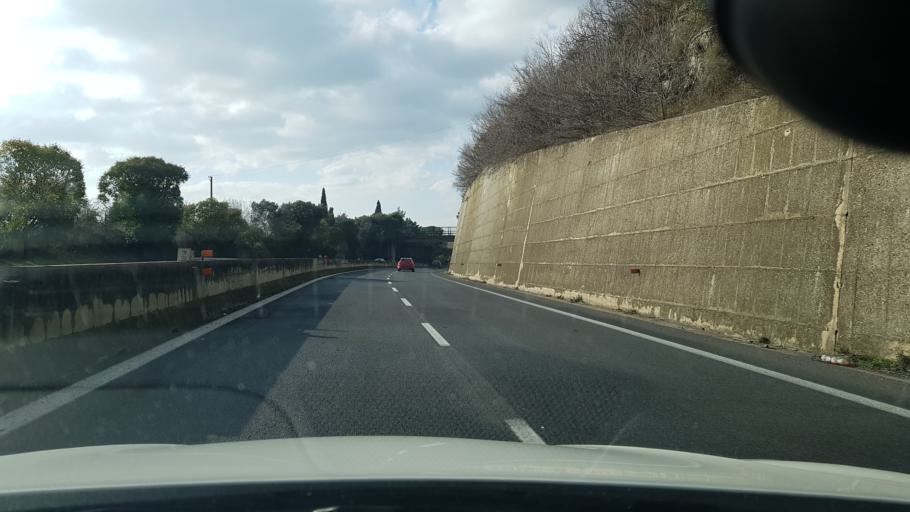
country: IT
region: Umbria
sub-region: Provincia di Perugia
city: Tuoro sul Trasimeno
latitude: 43.1914
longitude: 12.0500
